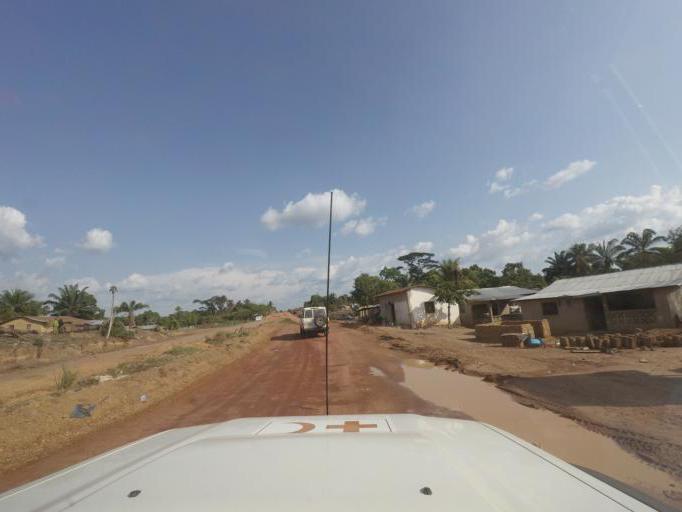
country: LR
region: Bong
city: Gbarnga
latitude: 7.0176
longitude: -9.4904
